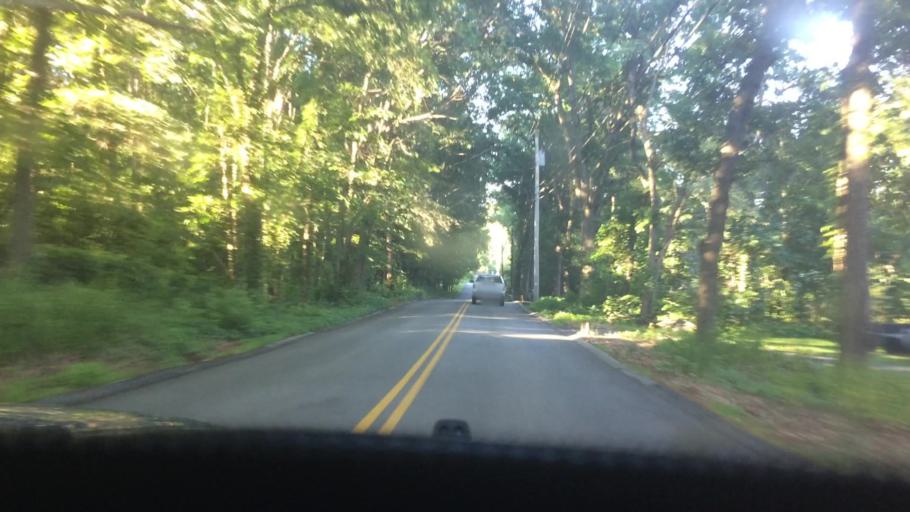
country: US
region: Massachusetts
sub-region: Middlesex County
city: North Reading
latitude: 42.6260
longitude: -71.0936
